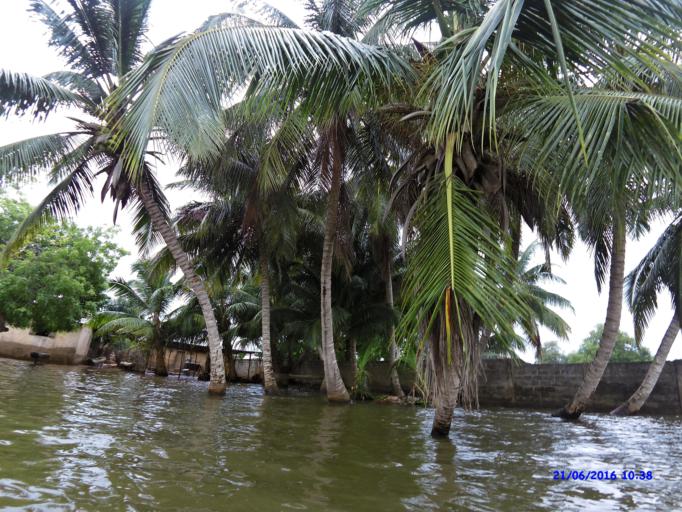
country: BJ
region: Mono
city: Come
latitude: 6.4836
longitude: 1.9484
